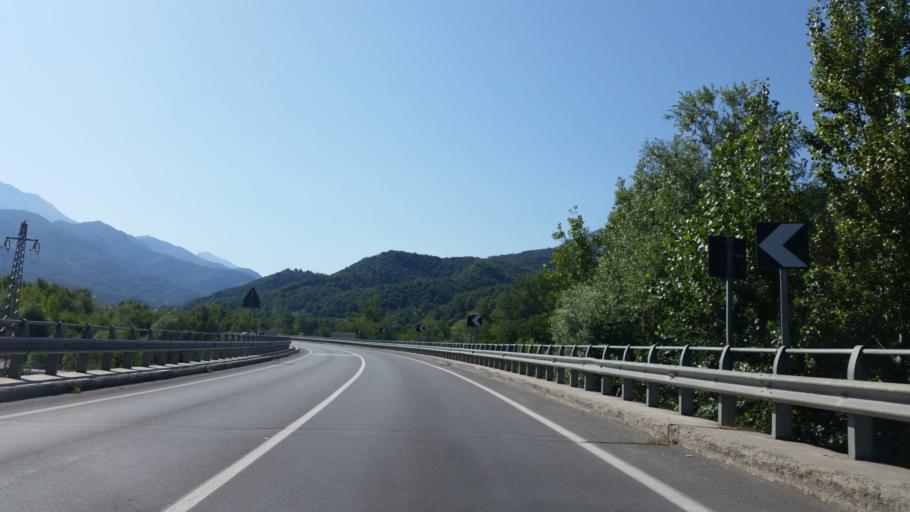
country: IT
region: Piedmont
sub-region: Provincia di Cuneo
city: Roccavione
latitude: 44.3155
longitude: 7.4878
